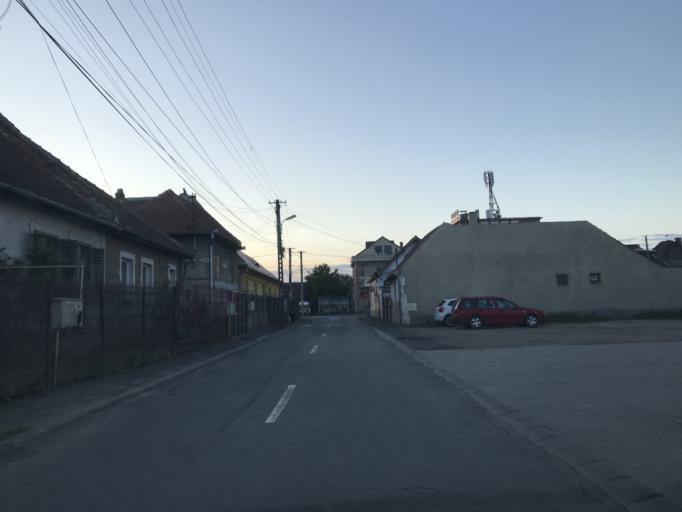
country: RO
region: Sibiu
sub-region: Municipiul Sibiu
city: Sibiu
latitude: 45.7996
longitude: 24.1671
